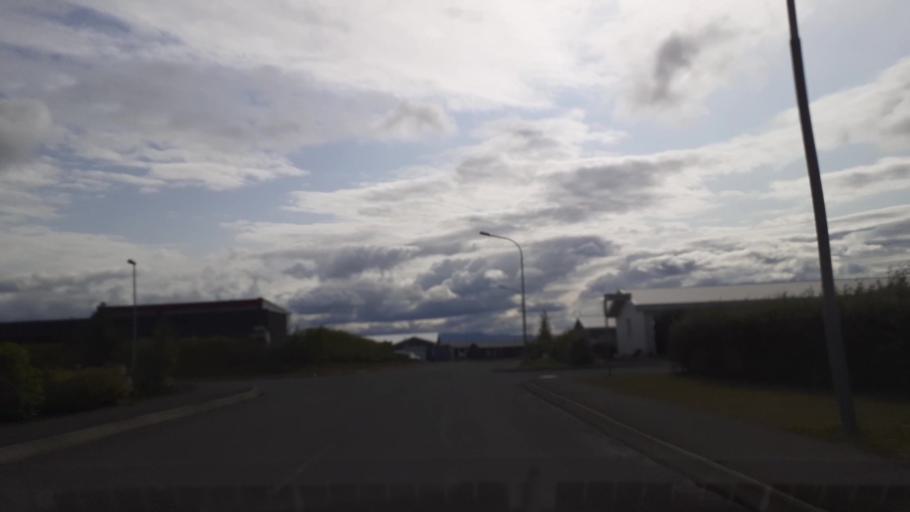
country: IS
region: South
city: Vestmannaeyjar
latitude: 63.8337
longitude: -20.3891
